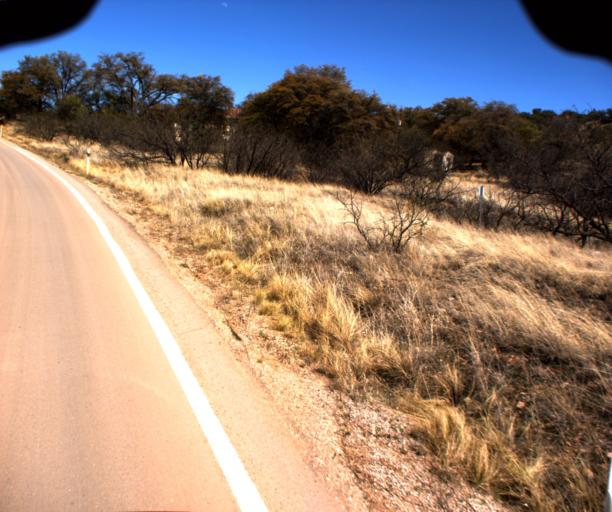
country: US
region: Arizona
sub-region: Cochise County
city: Huachuca City
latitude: 31.5419
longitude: -110.5117
